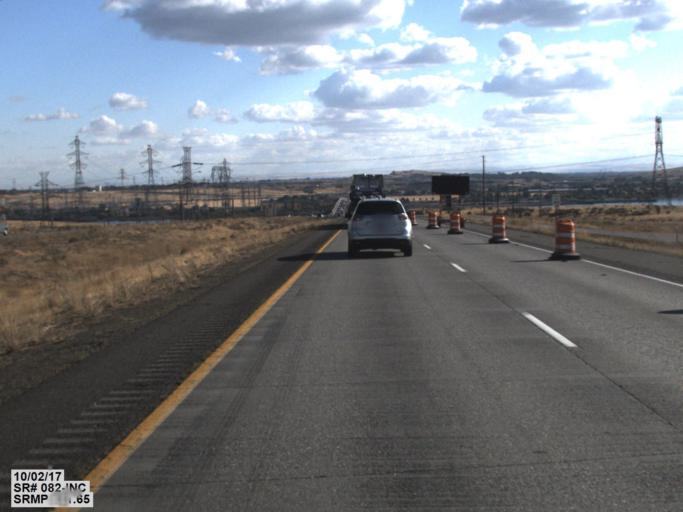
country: US
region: Oregon
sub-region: Umatilla County
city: Umatilla
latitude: 45.9448
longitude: -119.3351
